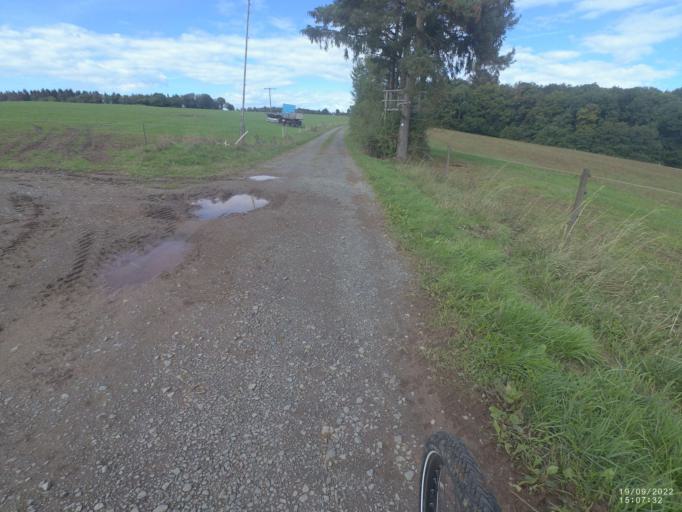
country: DE
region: Rheinland-Pfalz
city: Bleckhausen
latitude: 50.1414
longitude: 6.7683
